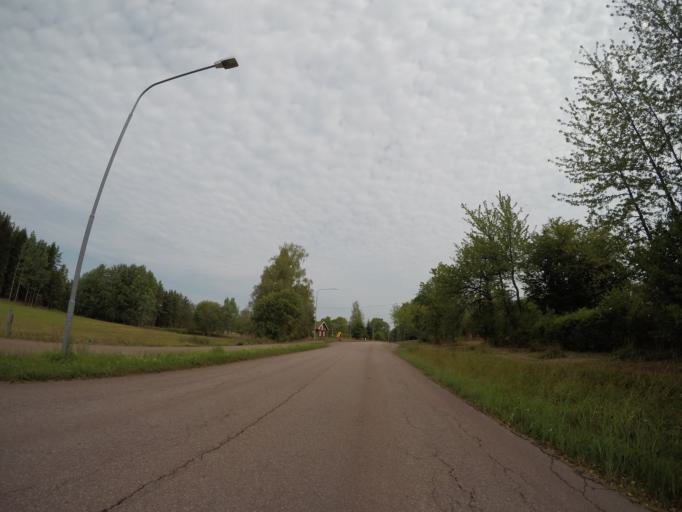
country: AX
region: Alands landsbygd
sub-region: Finstroem
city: Finstroem
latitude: 60.2176
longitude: 19.9795
